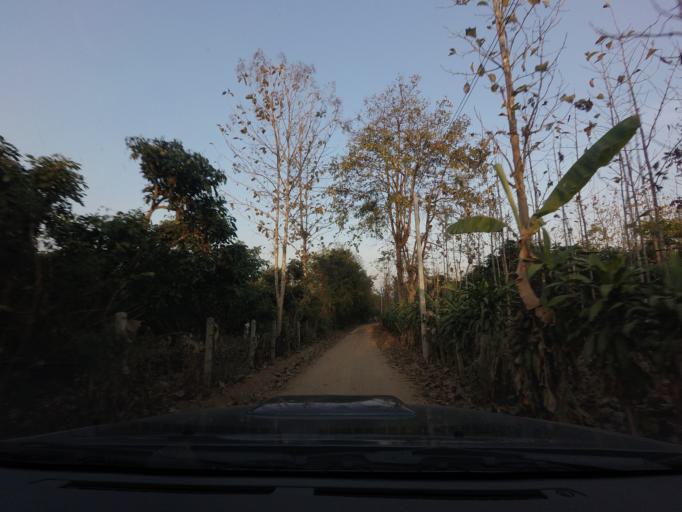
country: TH
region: Chiang Mai
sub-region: Amphoe Chiang Dao
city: Chiang Dao
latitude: 19.3649
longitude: 98.9355
